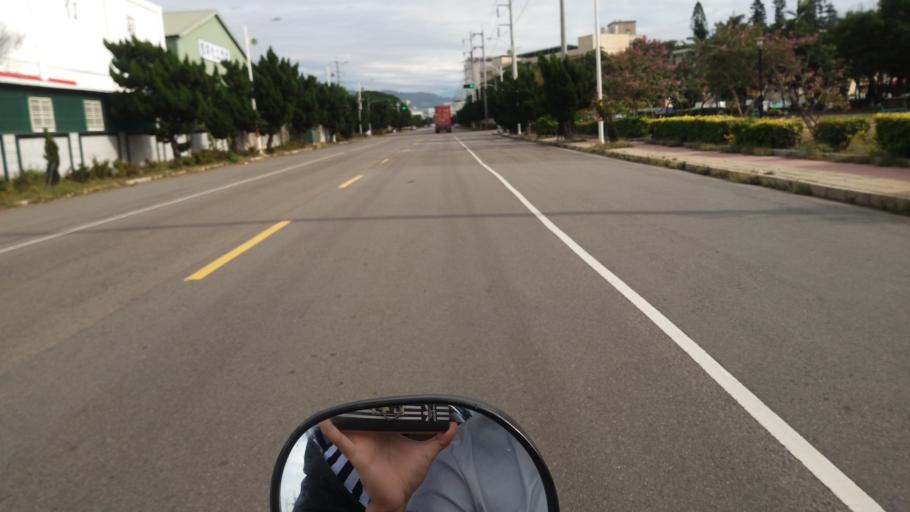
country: TW
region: Taiwan
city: Fengyuan
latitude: 24.4075
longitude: 120.6469
